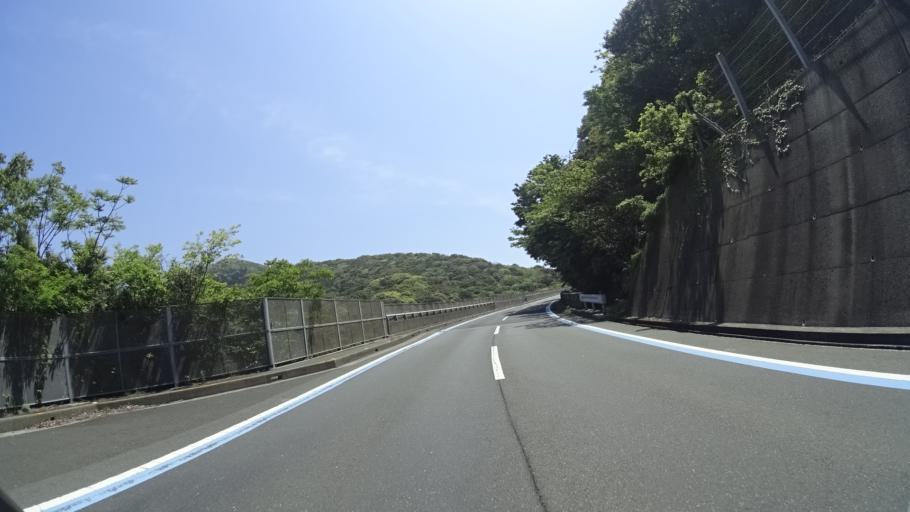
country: JP
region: Ehime
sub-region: Nishiuwa-gun
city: Ikata-cho
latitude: 33.4159
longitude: 132.1748
